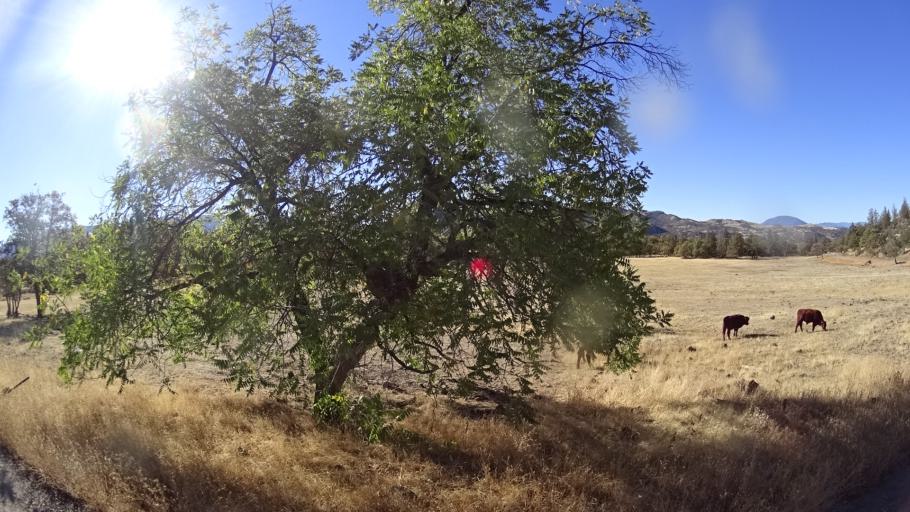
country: US
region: California
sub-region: Siskiyou County
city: Montague
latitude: 41.9898
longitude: -122.3458
